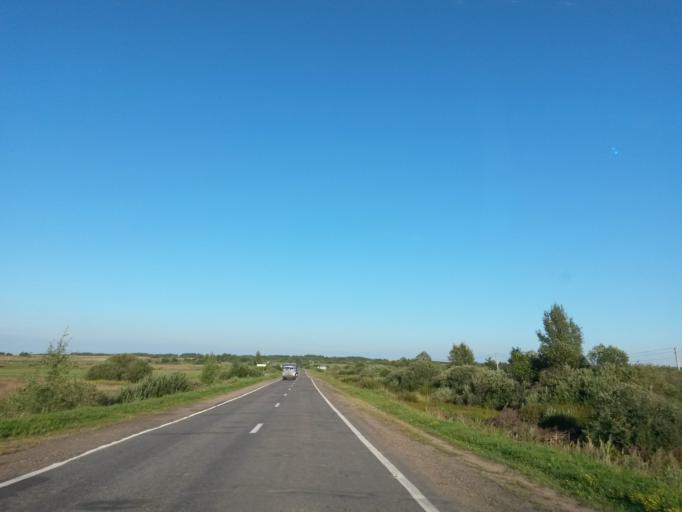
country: RU
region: Jaroslavl
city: Gavrilov-Yam
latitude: 57.3081
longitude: 39.8778
